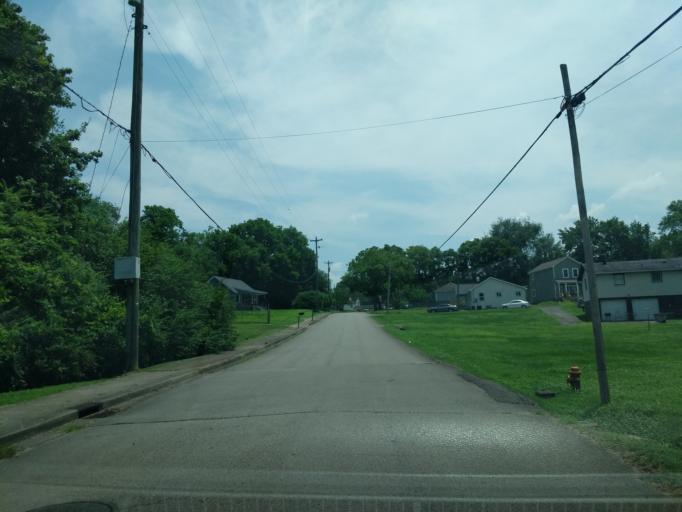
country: US
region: Tennessee
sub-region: Davidson County
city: Lakewood
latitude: 36.2275
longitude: -86.6301
